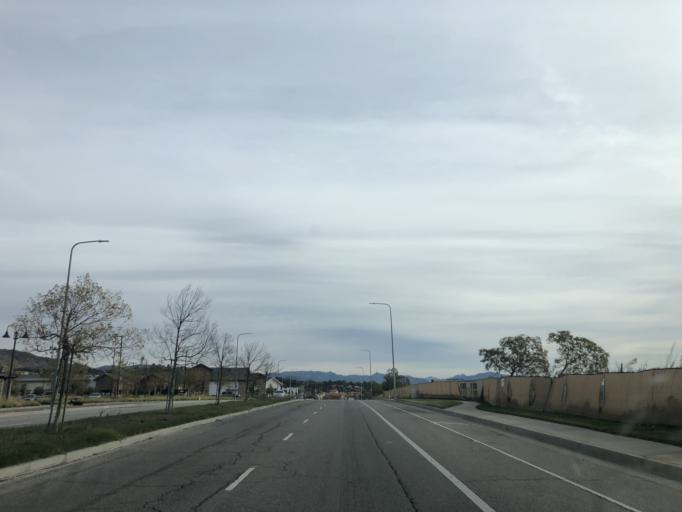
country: US
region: California
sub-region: Los Angeles County
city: Chatsworth
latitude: 34.2745
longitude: -118.5753
